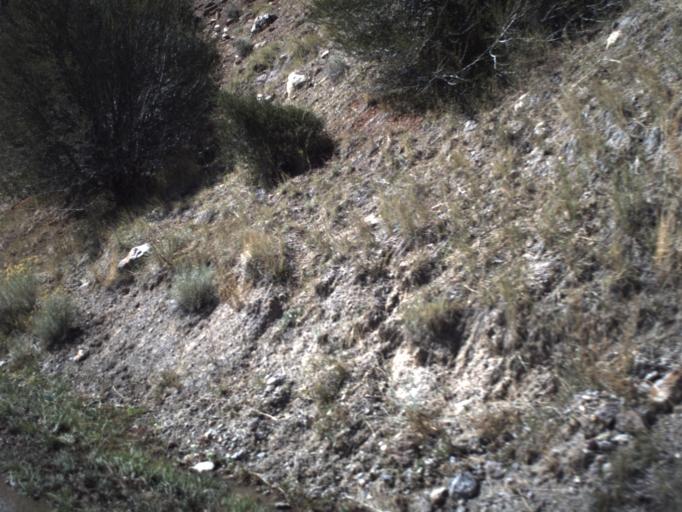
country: US
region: Utah
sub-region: Beaver County
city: Beaver
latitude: 38.2708
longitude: -112.4821
